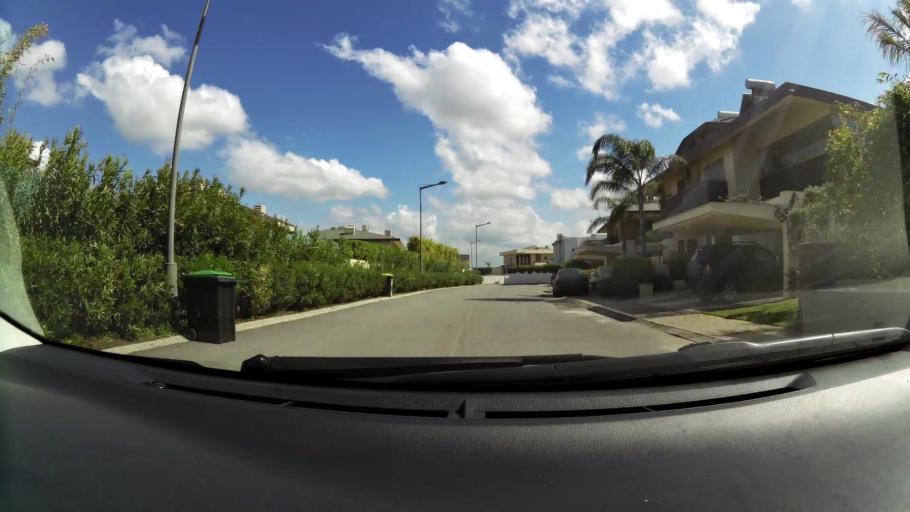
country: MA
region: Grand Casablanca
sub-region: Nouaceur
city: Bouskoura
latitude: 33.4674
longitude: -7.5955
